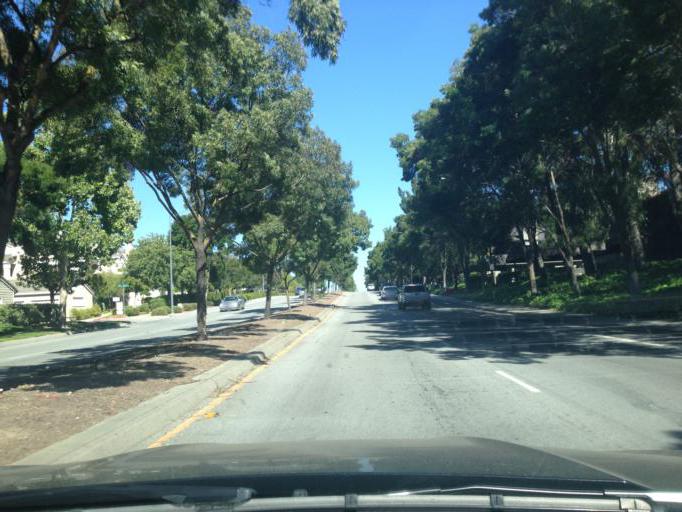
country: US
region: California
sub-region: Santa Clara County
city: Seven Trees
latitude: 37.2427
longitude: -121.8680
